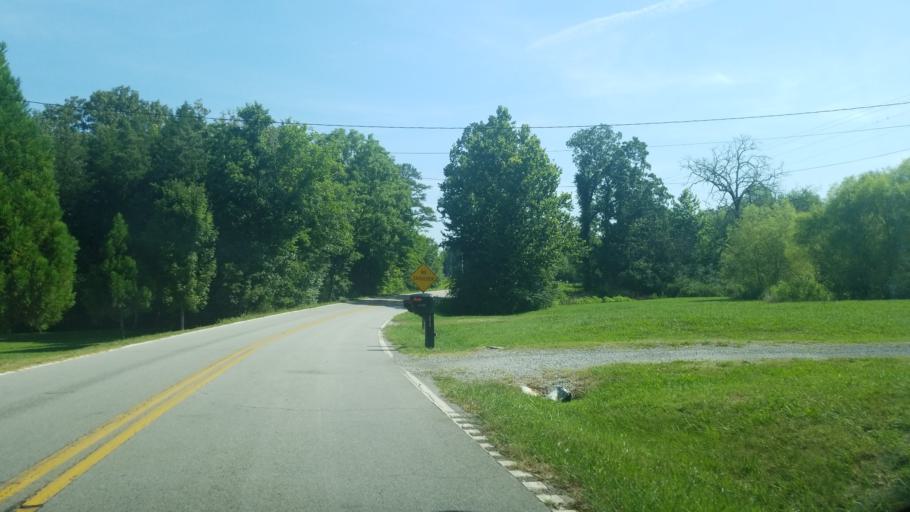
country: US
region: Tennessee
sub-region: Hamilton County
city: Sale Creek
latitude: 35.2965
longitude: -85.0396
